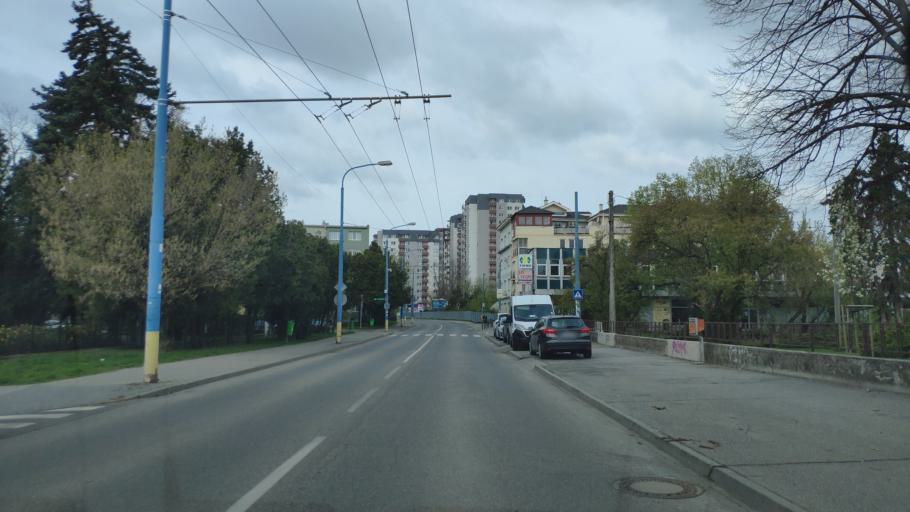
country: SK
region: Bratislavsky
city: Bratislava
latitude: 48.1499
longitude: 17.1721
